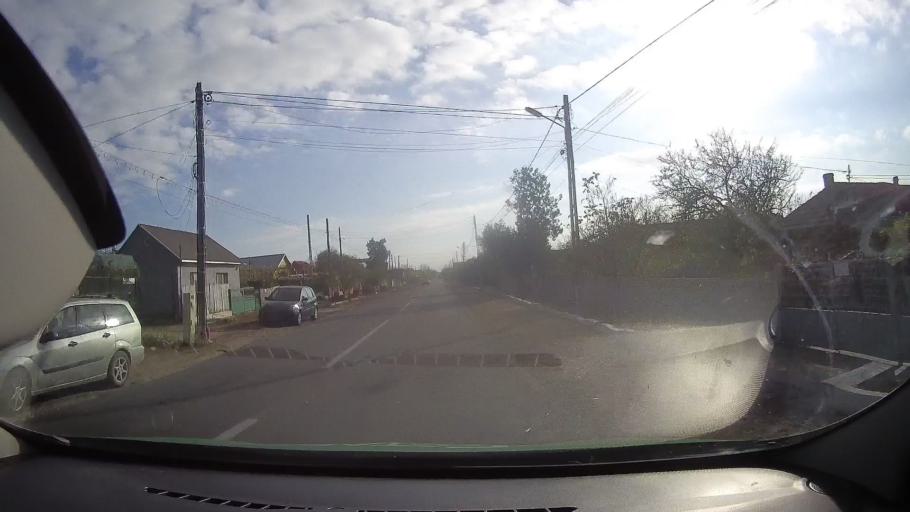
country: RO
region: Constanta
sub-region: Comuna Corbu
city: Corbu
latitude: 44.4047
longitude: 28.6615
